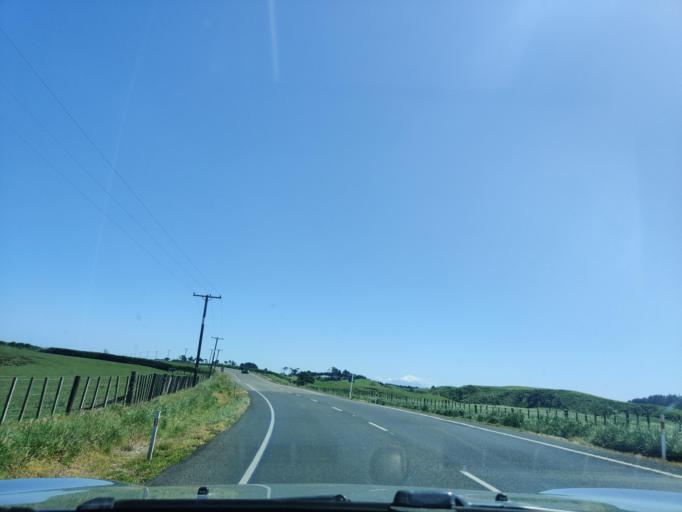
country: NZ
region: Taranaki
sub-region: South Taranaki District
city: Patea
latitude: -39.7494
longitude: 174.5366
